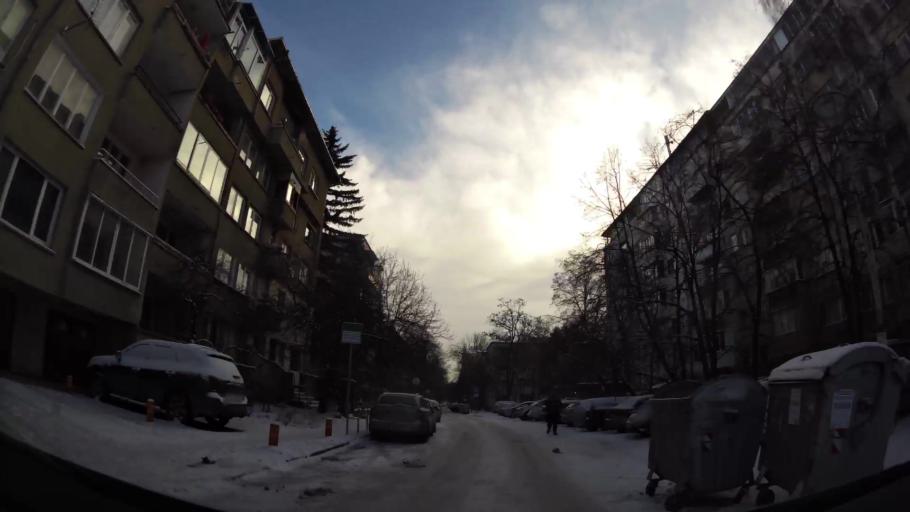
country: BG
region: Sofia-Capital
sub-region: Stolichna Obshtina
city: Sofia
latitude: 42.6698
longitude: 23.3228
